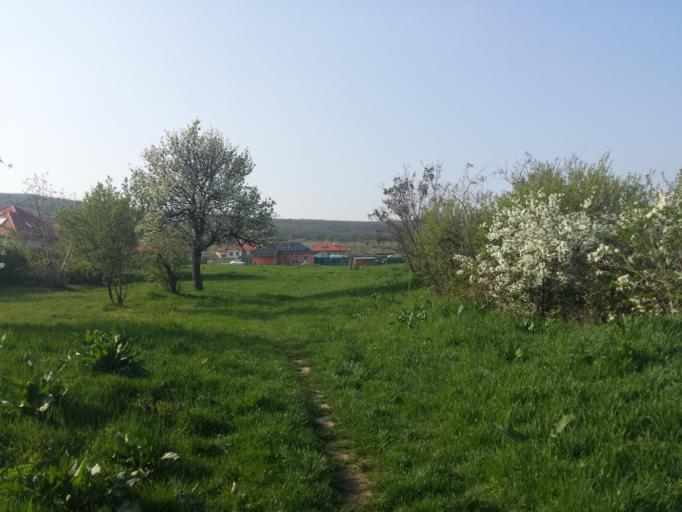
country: HU
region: Fejer
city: Velence
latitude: 47.2600
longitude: 18.6224
